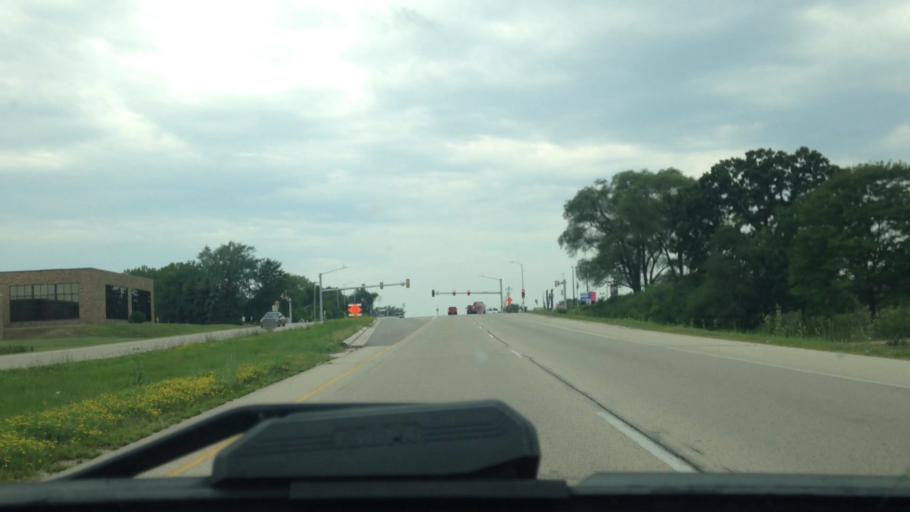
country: US
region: Wisconsin
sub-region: Waukesha County
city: Butler
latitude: 43.1192
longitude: -88.0828
